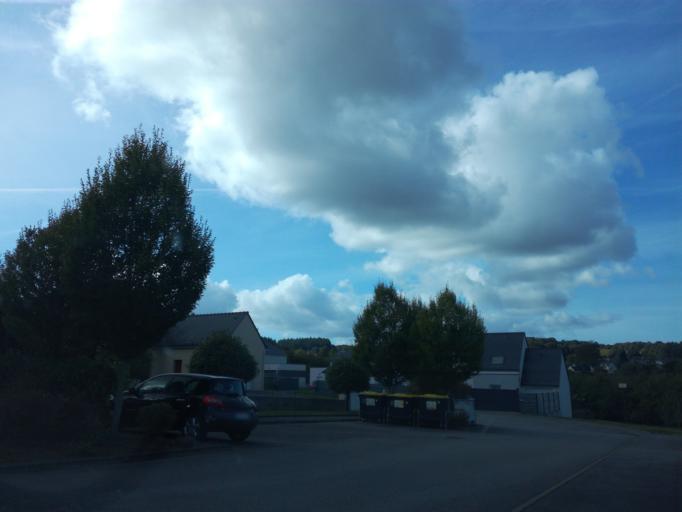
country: FR
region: Brittany
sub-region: Departement du Morbihan
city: Le Sourn
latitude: 48.0437
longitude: -2.9825
